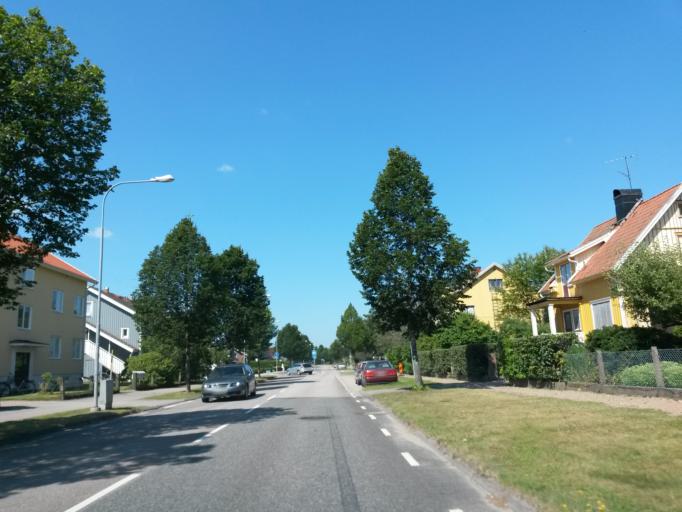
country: SE
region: Vaestra Goetaland
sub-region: Vargarda Kommun
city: Vargarda
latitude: 58.0332
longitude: 12.8013
